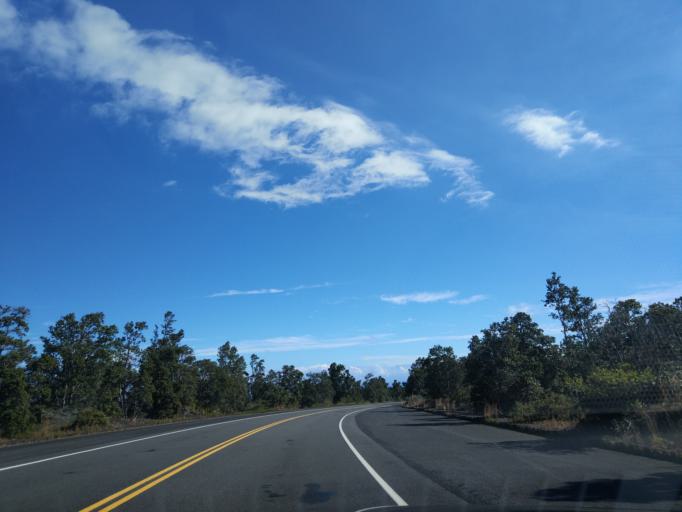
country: US
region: Hawaii
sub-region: Hawaii County
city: Volcano
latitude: 19.3455
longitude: -155.2129
